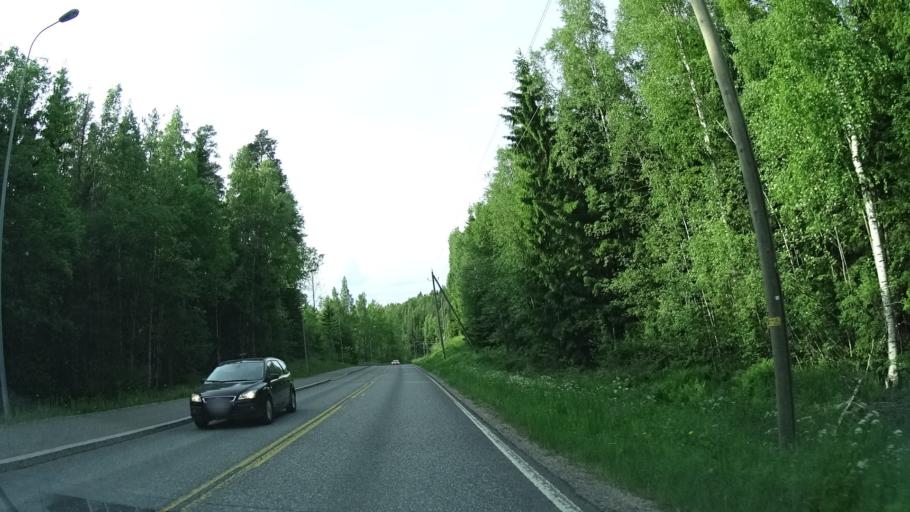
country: FI
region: Uusimaa
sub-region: Helsinki
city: Espoo
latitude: 60.2722
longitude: 24.5937
